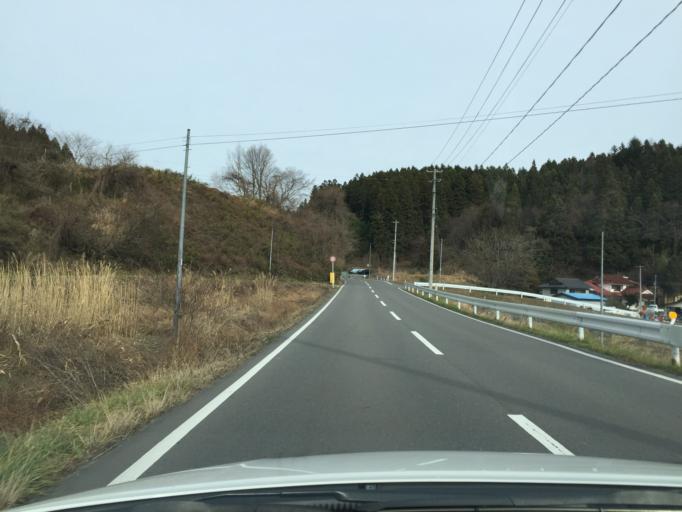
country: JP
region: Fukushima
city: Ishikawa
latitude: 37.2193
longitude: 140.6298
